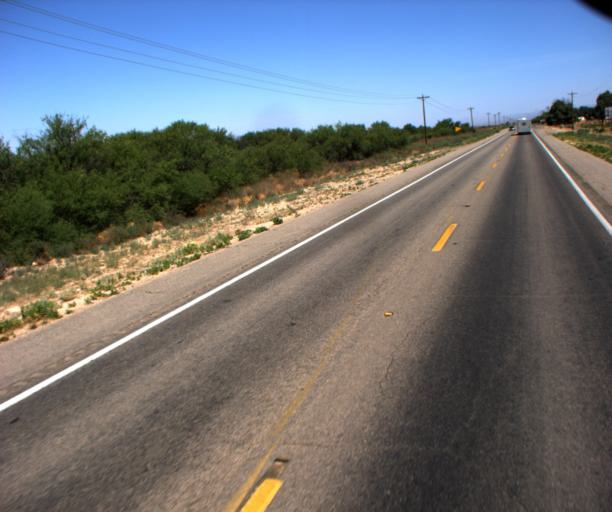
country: US
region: Arizona
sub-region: Graham County
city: Pima
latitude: 32.9582
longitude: -109.9180
